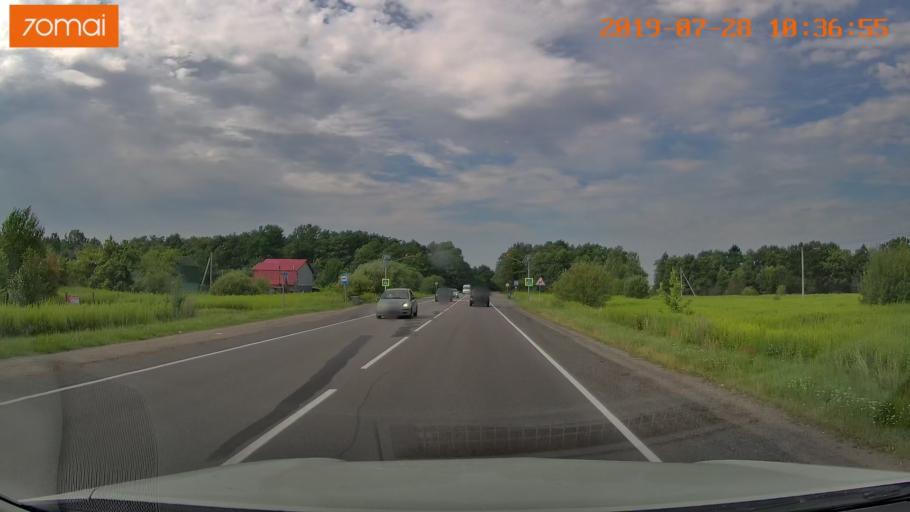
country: RU
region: Kaliningrad
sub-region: Gorod Kaliningrad
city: Kaliningrad
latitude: 54.7348
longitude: 20.4159
